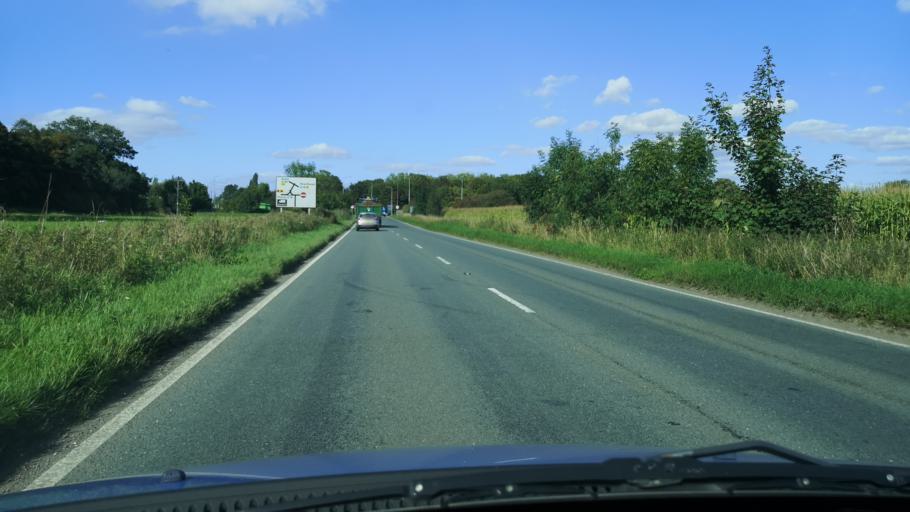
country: GB
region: England
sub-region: North Lincolnshire
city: Crowle
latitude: 53.5836
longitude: -0.8199
